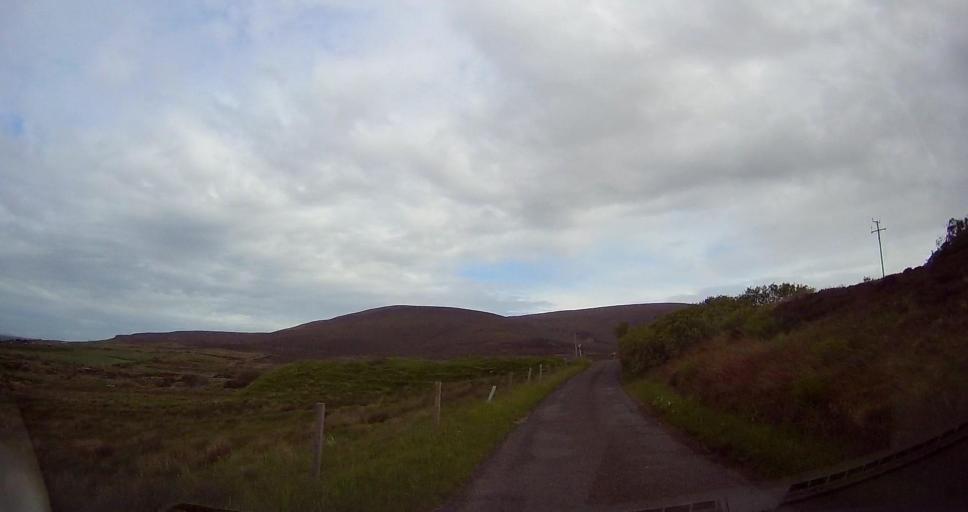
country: GB
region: Scotland
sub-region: Orkney Islands
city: Stromness
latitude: 58.9067
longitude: -3.3177
